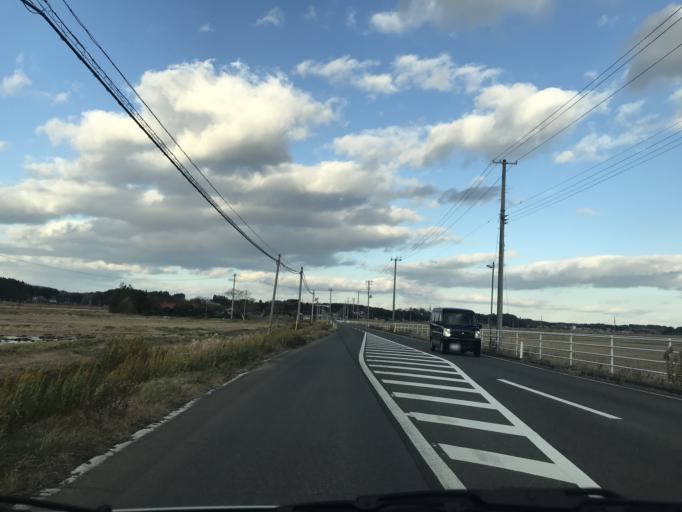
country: JP
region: Miyagi
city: Kogota
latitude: 38.6439
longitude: 141.0529
